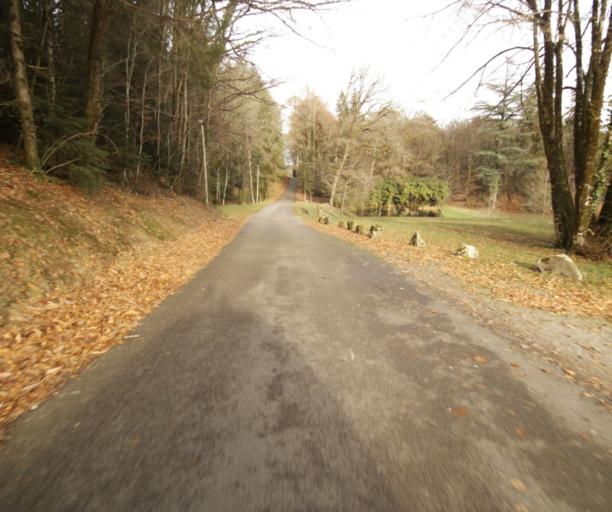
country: FR
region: Limousin
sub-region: Departement de la Correze
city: Saint-Mexant
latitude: 45.2589
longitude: 1.6668
